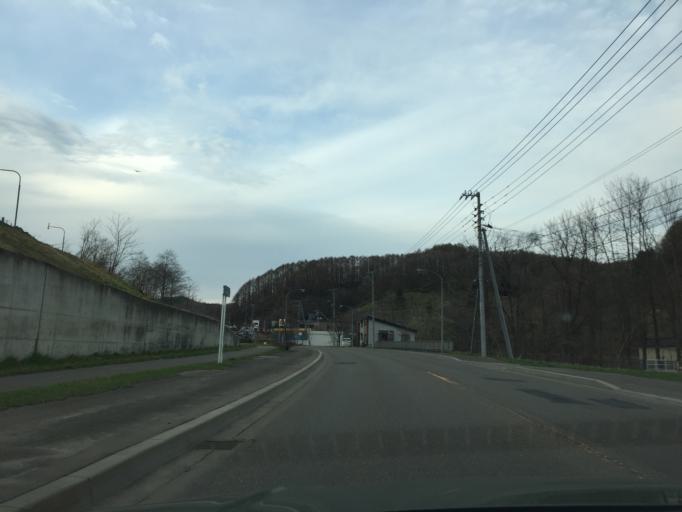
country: JP
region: Hokkaido
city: Utashinai
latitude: 43.5116
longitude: 142.0262
